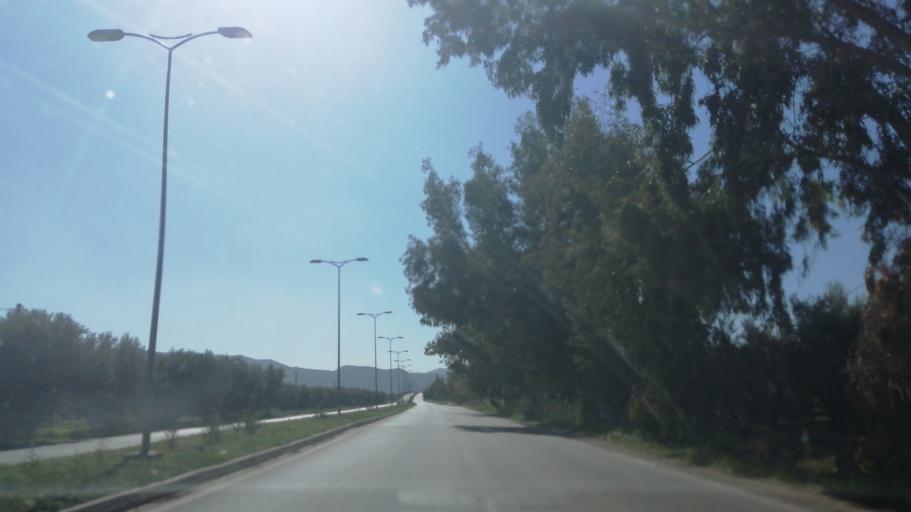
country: DZ
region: Mascara
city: Sig
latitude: 35.5454
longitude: -0.2052
